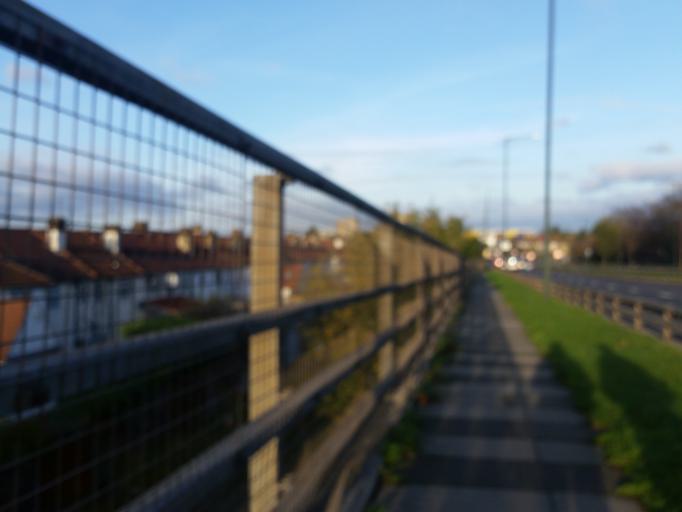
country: GB
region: England
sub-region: Greater London
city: Enfield
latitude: 51.6380
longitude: -0.0658
